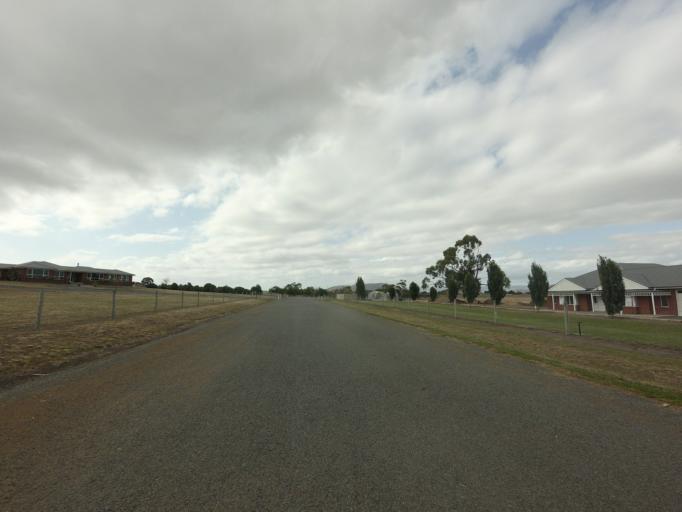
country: AU
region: Tasmania
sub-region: Clarence
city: Cambridge
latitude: -42.8388
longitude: 147.4693
